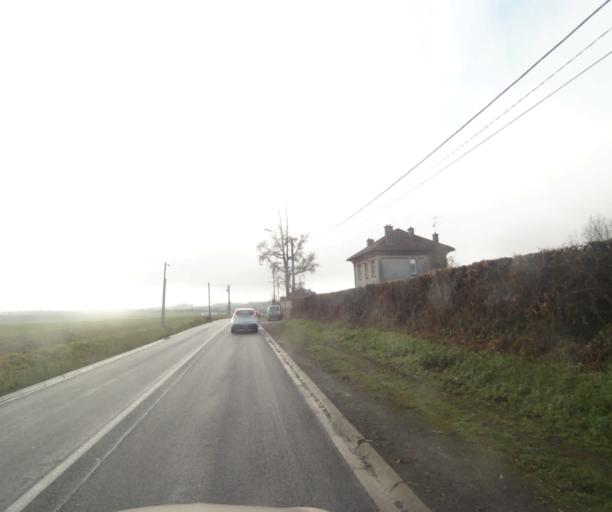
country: FR
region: Nord-Pas-de-Calais
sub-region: Departement du Nord
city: Famars
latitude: 50.3036
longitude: 3.5172
